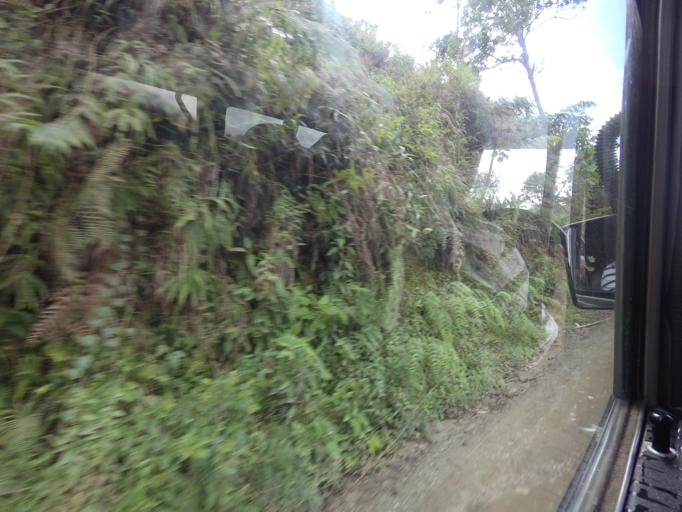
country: CO
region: Huila
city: Isnos
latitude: 1.9522
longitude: -76.2795
